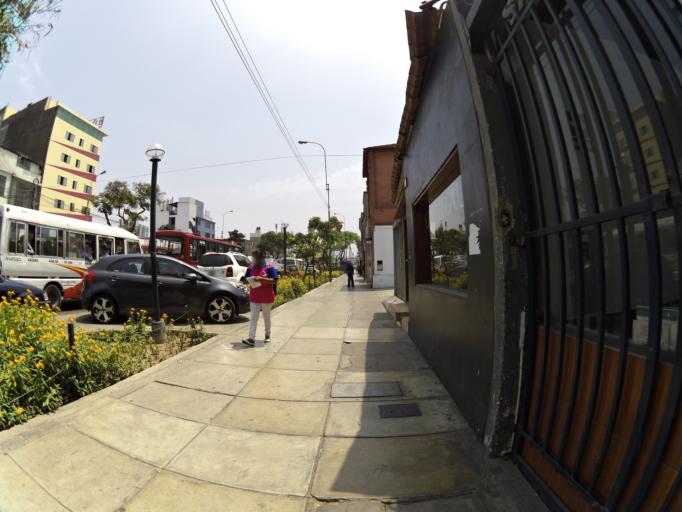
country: PE
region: Lima
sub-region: Lima
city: San Isidro
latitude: -12.1138
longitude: -77.0281
